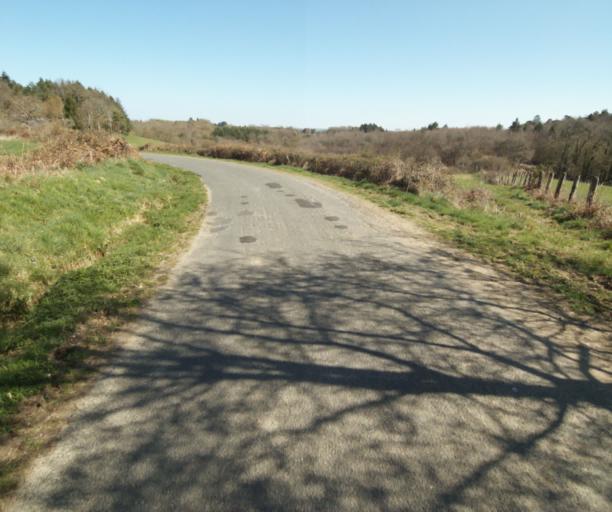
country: FR
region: Limousin
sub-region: Departement de la Correze
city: Chameyrat
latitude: 45.2841
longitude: 1.7019
